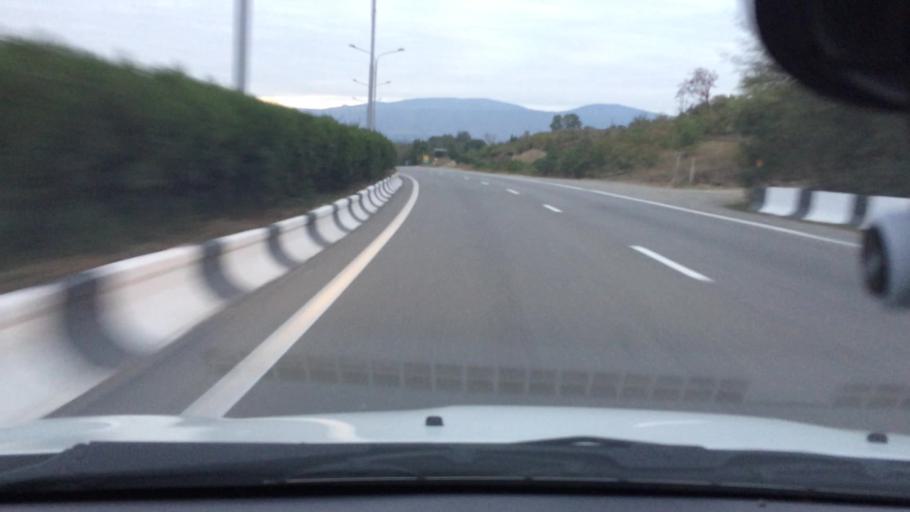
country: GE
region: Mtskheta-Mtianeti
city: Mtskheta
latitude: 41.8680
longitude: 44.7306
